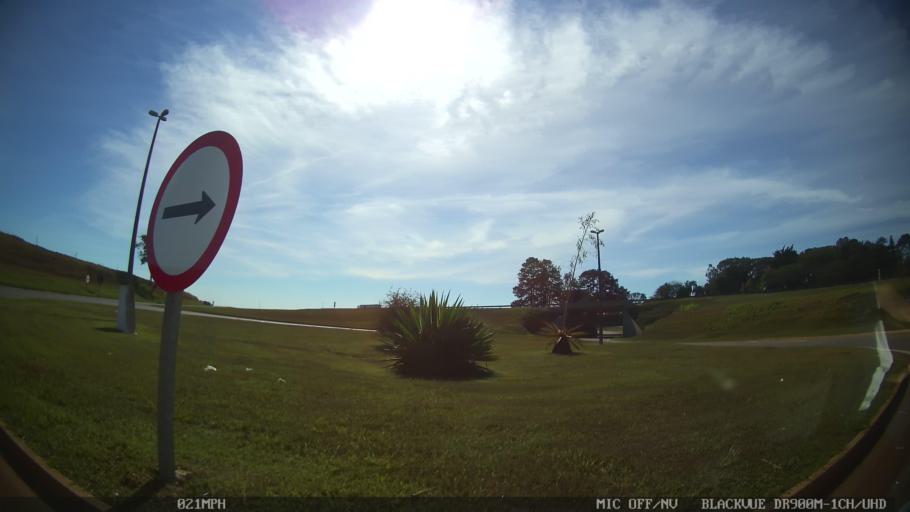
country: BR
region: Sao Paulo
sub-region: Leme
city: Leme
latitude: -22.1485
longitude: -47.4037
